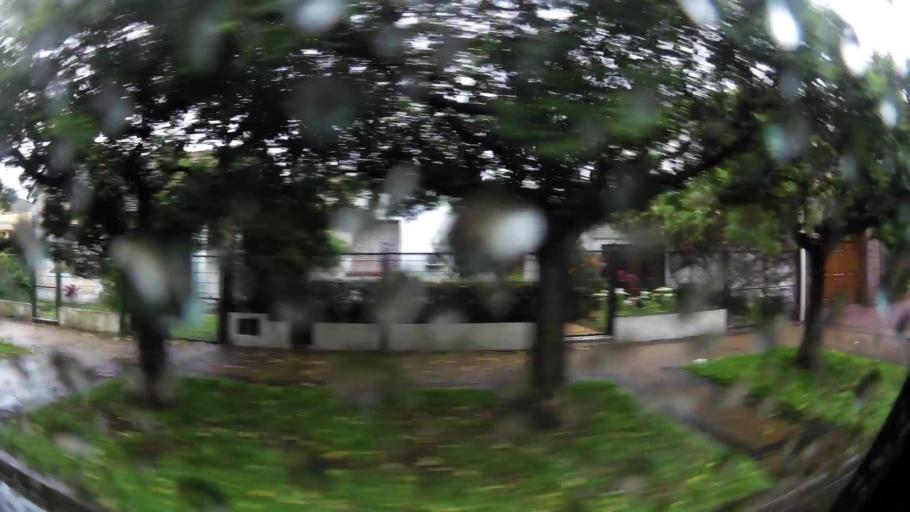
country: AR
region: Buenos Aires
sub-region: Partido de Lanus
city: Lanus
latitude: -34.7218
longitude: -58.3952
